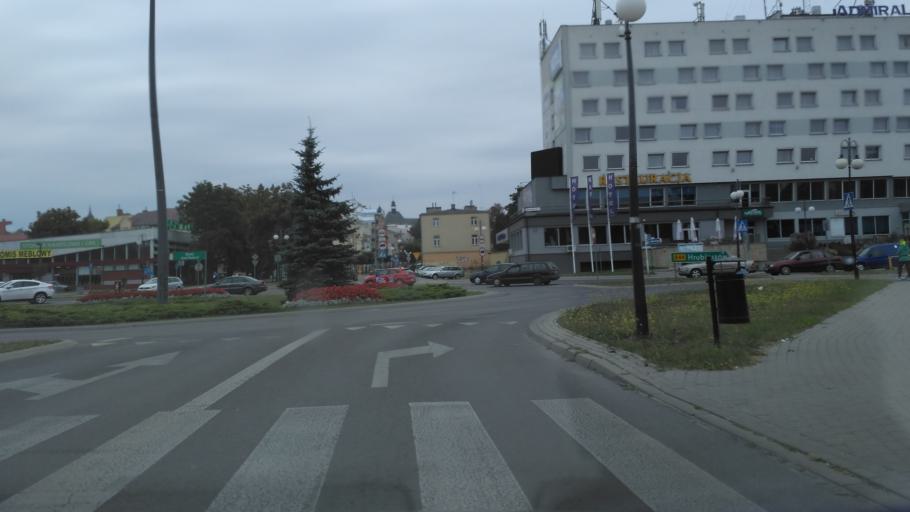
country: PL
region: Lublin Voivodeship
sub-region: Chelm
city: Chelm
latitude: 51.1364
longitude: 23.4666
